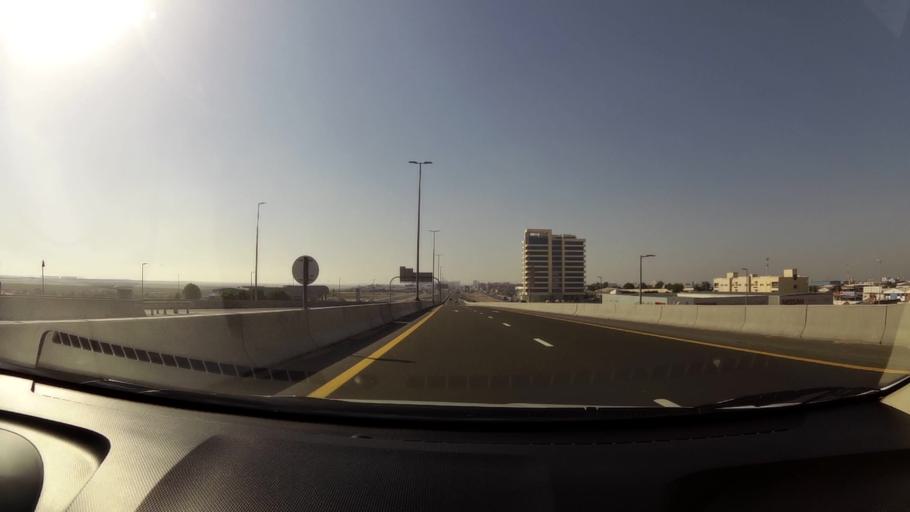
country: AE
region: Umm al Qaywayn
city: Umm al Qaywayn
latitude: 25.4957
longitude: 55.5527
